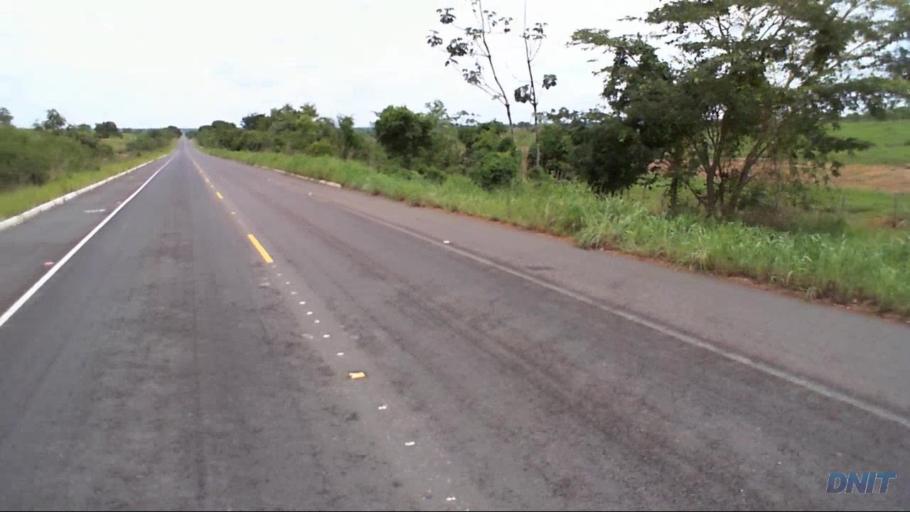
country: BR
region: Goias
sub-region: Sao Miguel Do Araguaia
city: Sao Miguel do Araguaia
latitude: -13.2974
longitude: -50.2449
